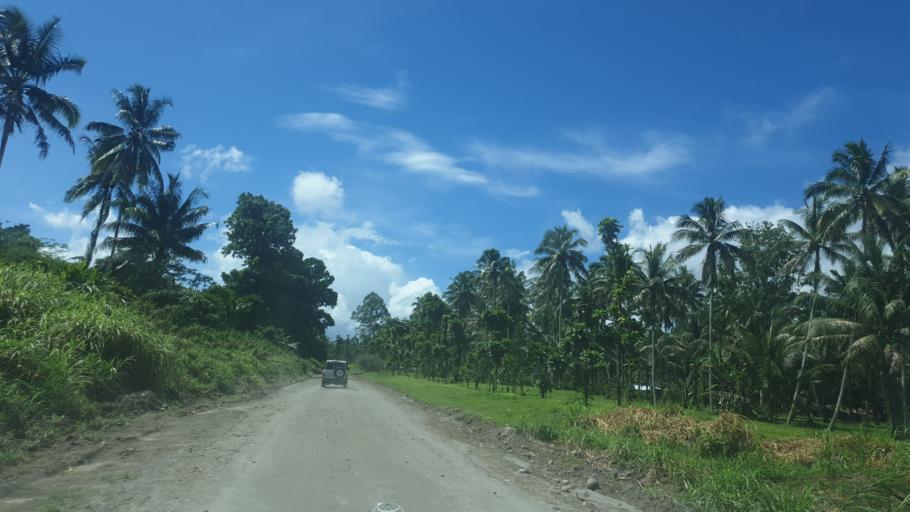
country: PG
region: Bougainville
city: Panguna
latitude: -6.6603
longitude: 155.4423
